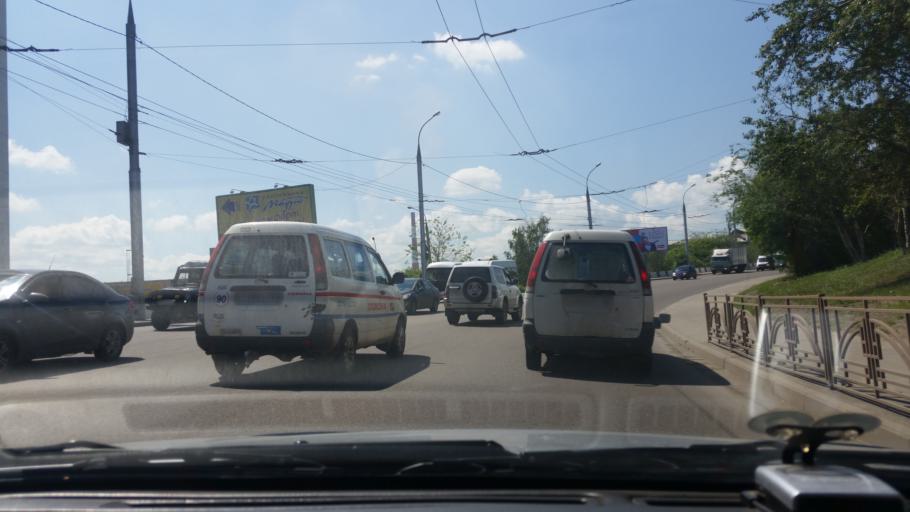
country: RU
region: Irkutsk
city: Smolenshchina
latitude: 52.2608
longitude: 104.2033
